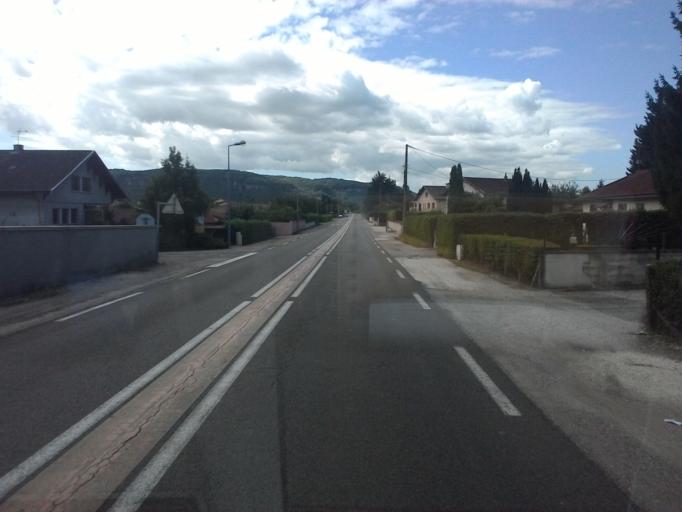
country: FR
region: Rhone-Alpes
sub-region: Departement de l'Ain
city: Lagnieu
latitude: 45.8929
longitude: 5.3476
